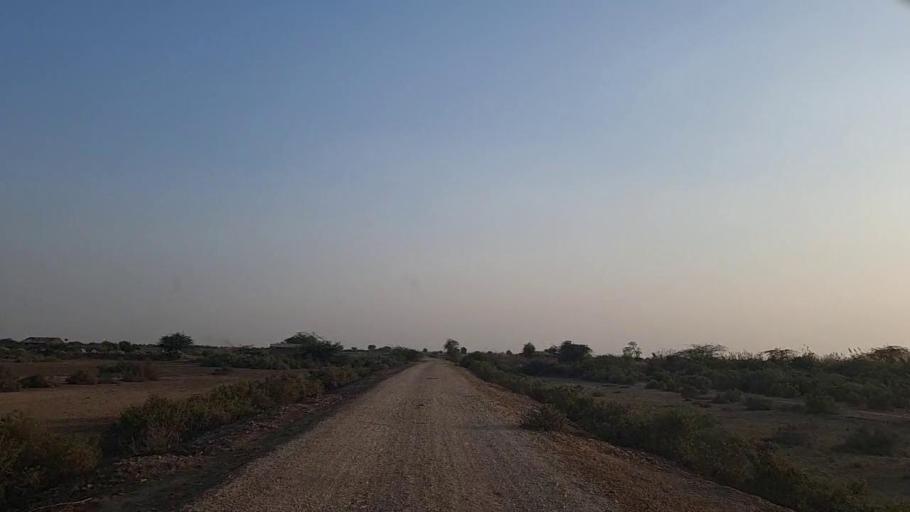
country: PK
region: Sindh
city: Jati
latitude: 24.4875
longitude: 68.4152
